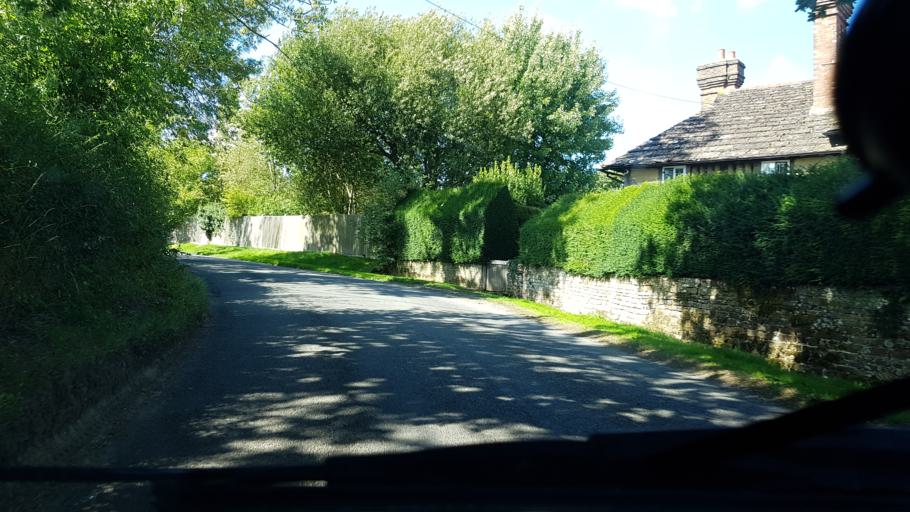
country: GB
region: England
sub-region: West Sussex
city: Horsham
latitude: 51.0941
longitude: -0.3474
